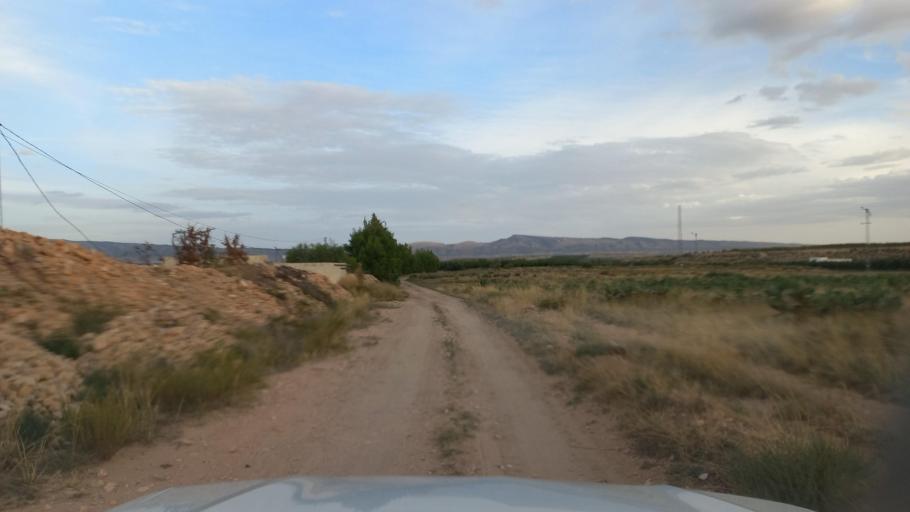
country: TN
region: Al Qasrayn
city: Sbiba
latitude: 35.4250
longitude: 9.0965
